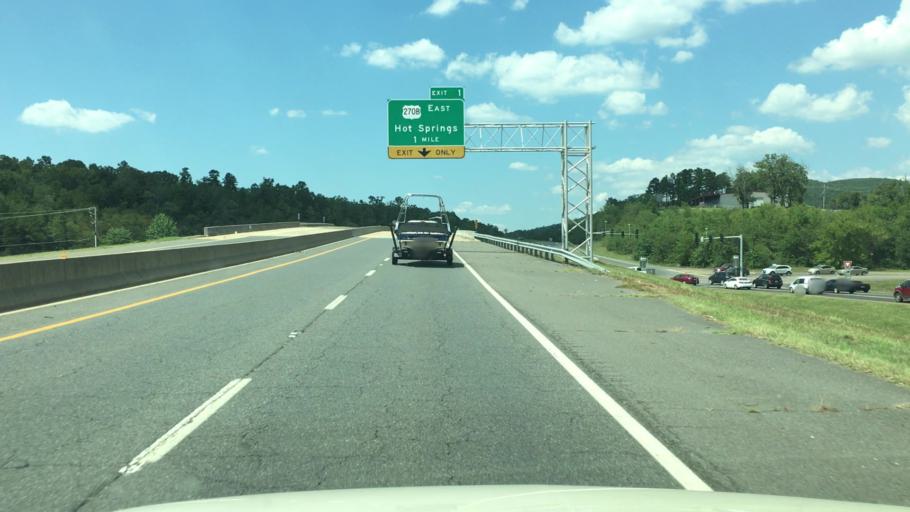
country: US
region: Arkansas
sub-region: Garland County
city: Rockwell
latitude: 34.4769
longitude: -93.1148
